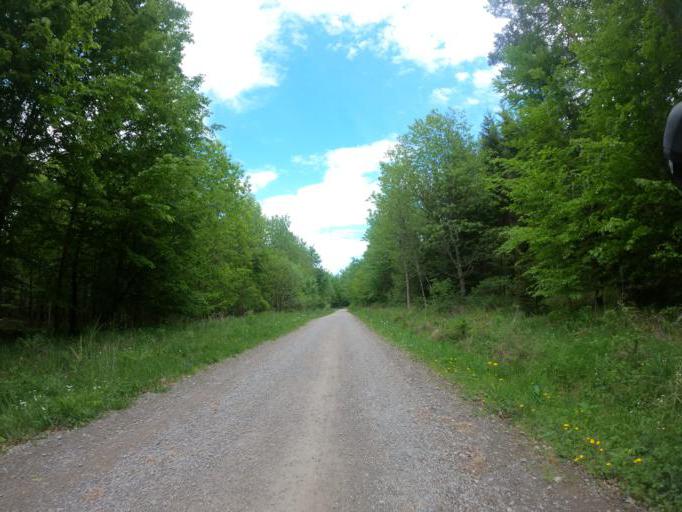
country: DE
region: Baden-Wuerttemberg
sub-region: Regierungsbezirk Stuttgart
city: Schonaich
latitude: 48.6508
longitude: 9.0383
